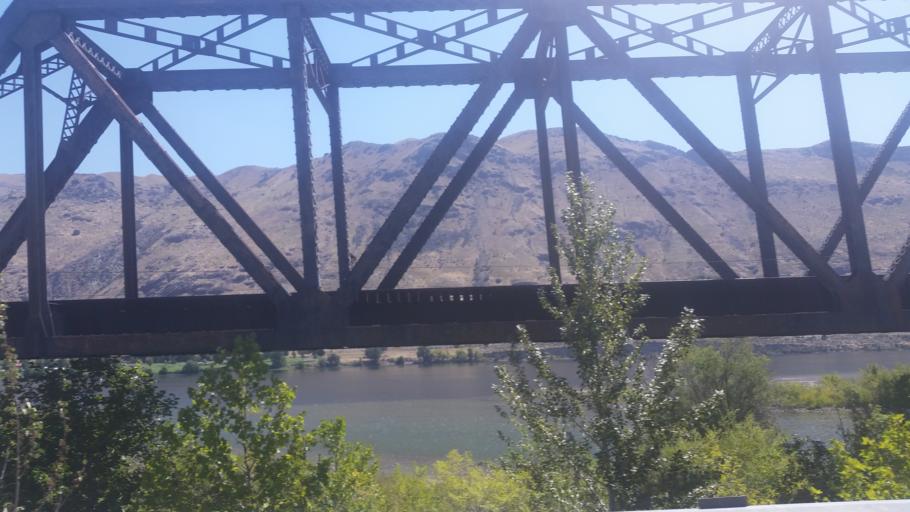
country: US
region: Washington
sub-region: Chelan County
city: Chelan
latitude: 47.8047
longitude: -119.9843
